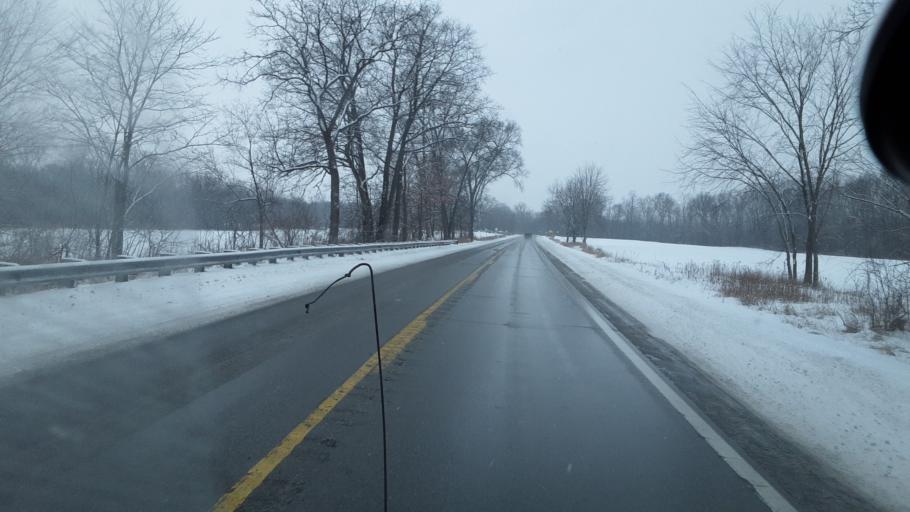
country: US
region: Michigan
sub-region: Jackson County
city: Jackson
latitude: 42.3254
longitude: -84.3656
